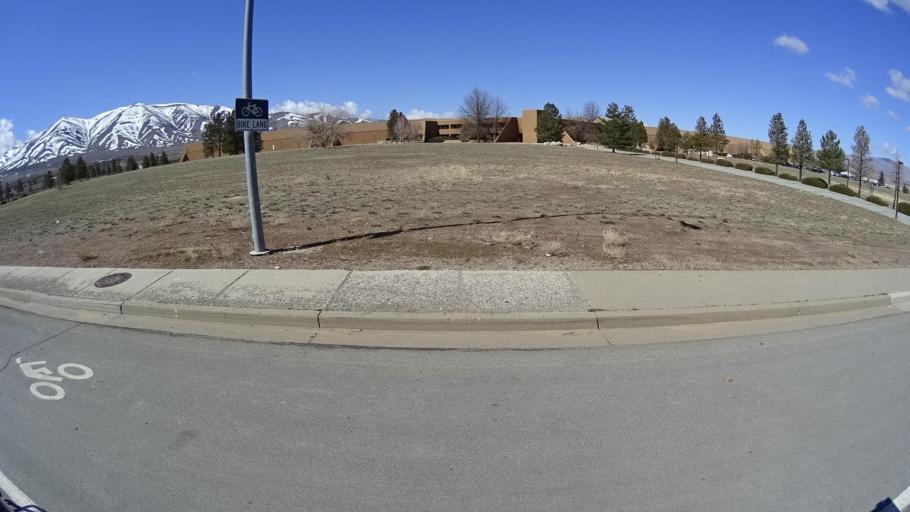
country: US
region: Nevada
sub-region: Washoe County
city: Lemmon Valley
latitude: 39.6366
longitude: -119.8820
